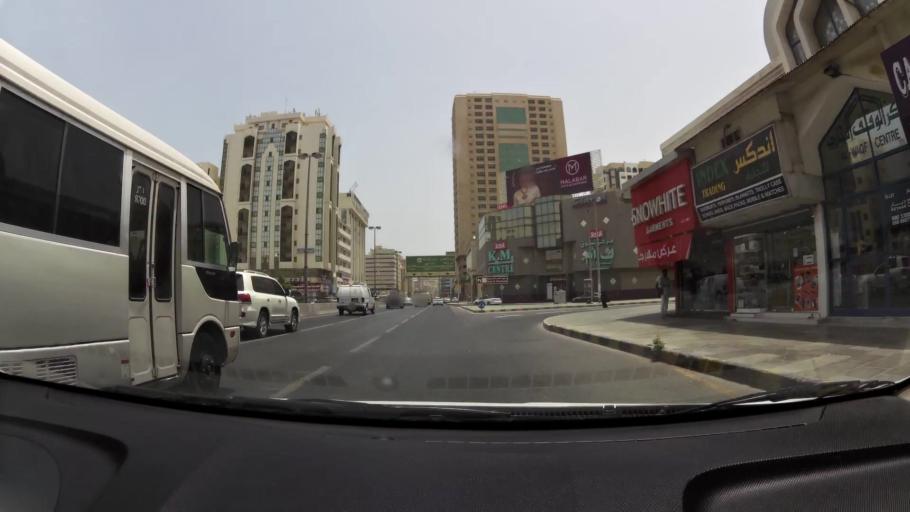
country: AE
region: Ash Shariqah
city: Sharjah
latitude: 25.3553
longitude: 55.3867
